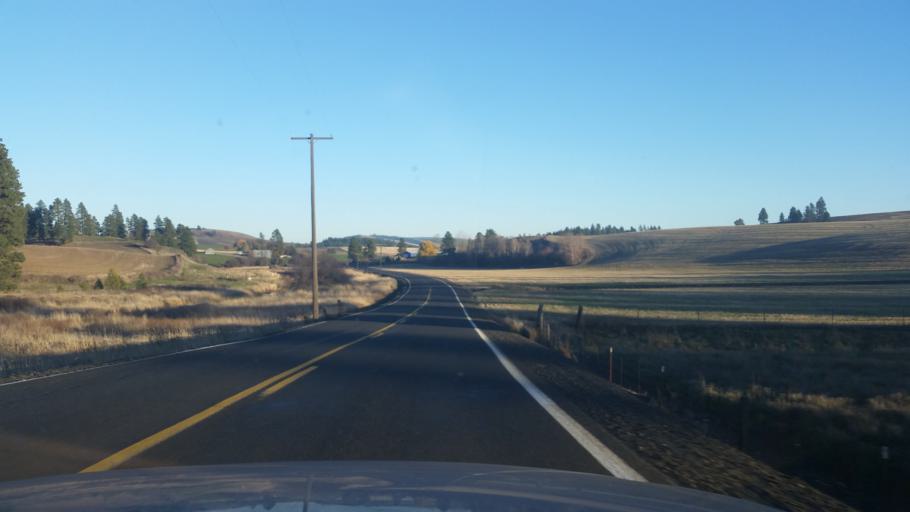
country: US
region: Washington
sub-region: Spokane County
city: Opportunity
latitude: 47.3528
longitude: -117.2568
